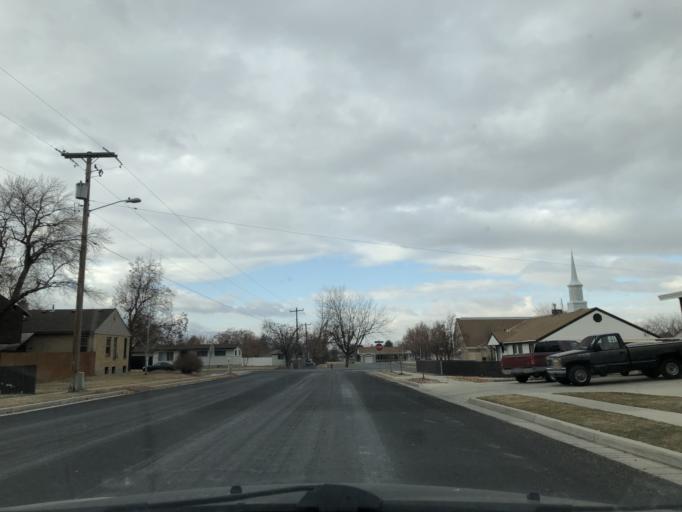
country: US
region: Utah
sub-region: Cache County
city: Logan
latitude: 41.7465
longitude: -111.8386
